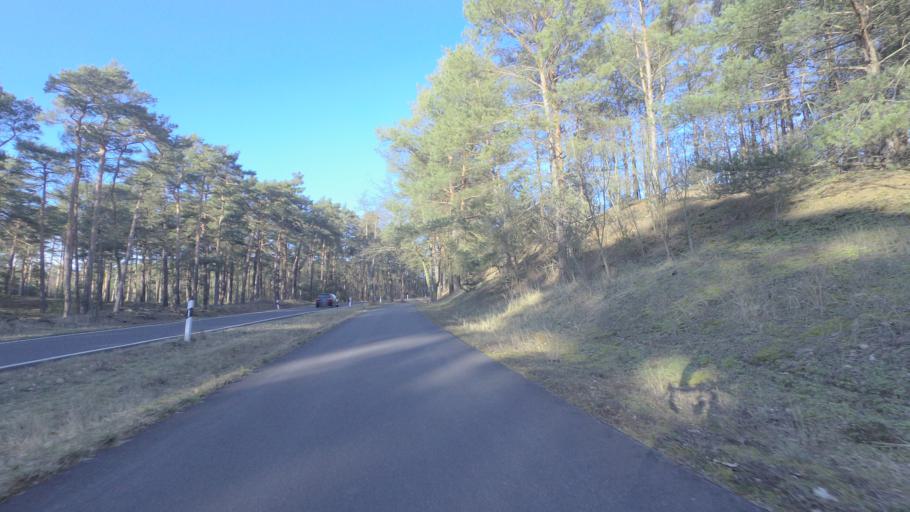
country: DE
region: Brandenburg
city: Sperenberg
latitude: 52.0372
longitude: 13.3189
